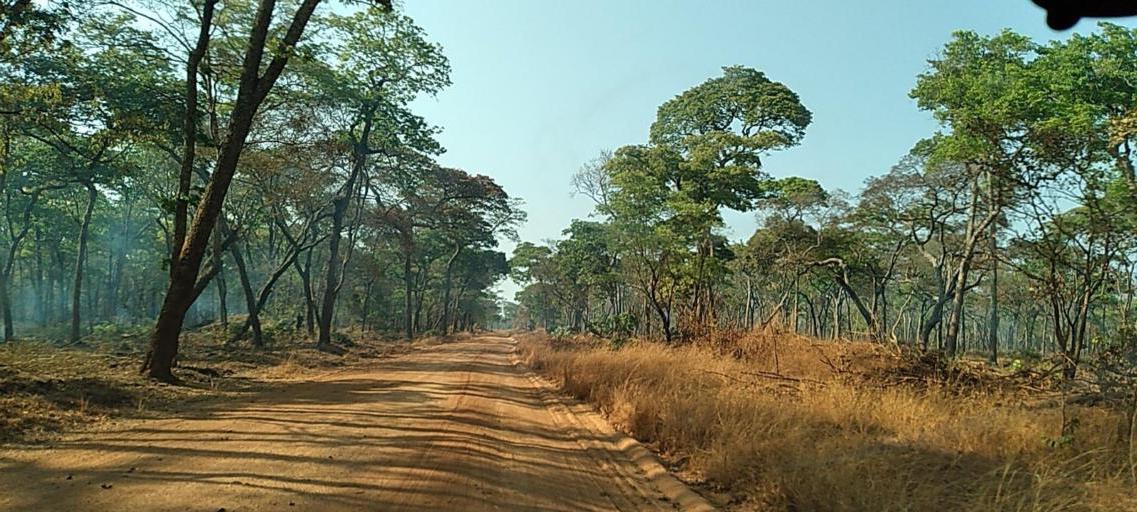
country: ZM
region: North-Western
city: Kasempa
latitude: -13.6177
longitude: 25.9798
